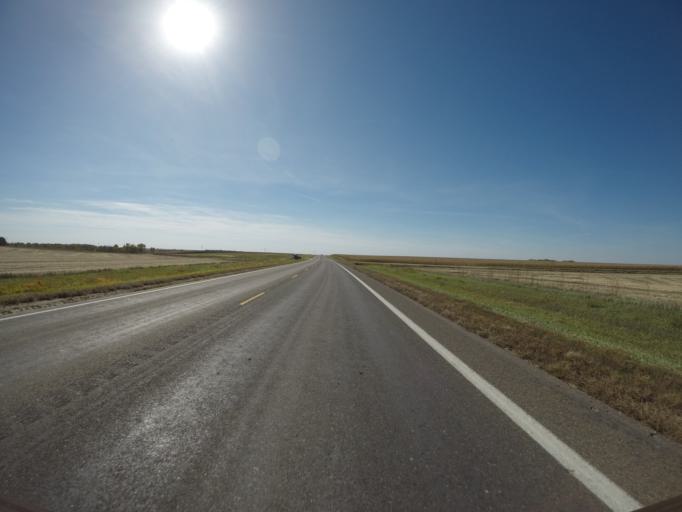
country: US
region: Kansas
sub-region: Smith County
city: Smith Center
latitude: 39.7815
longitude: -98.8034
